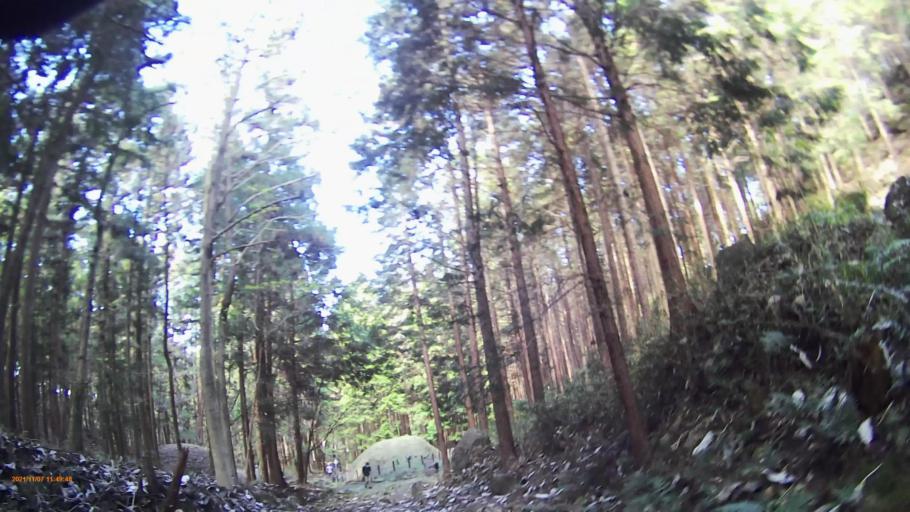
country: JP
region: Gifu
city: Mizunami
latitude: 35.4339
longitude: 137.2812
